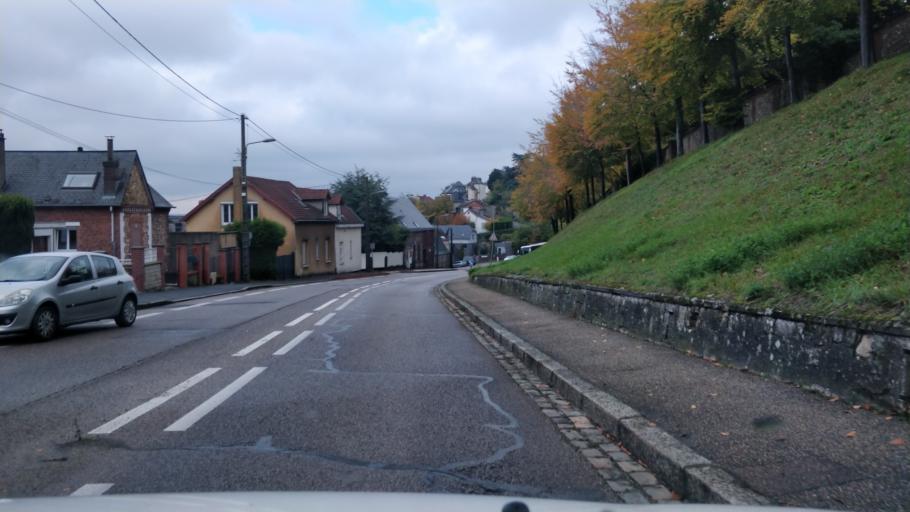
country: FR
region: Haute-Normandie
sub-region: Departement de la Seine-Maritime
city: Bihorel
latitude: 49.4488
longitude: 1.1160
